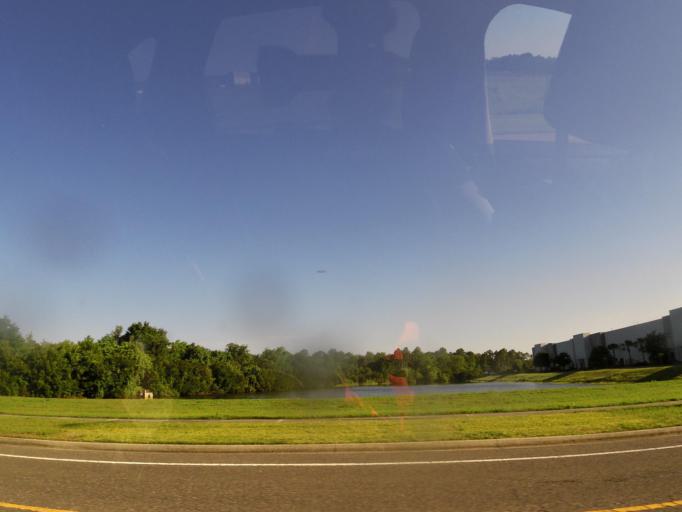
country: US
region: Florida
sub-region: Duval County
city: Jacksonville
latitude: 30.4508
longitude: -81.5621
